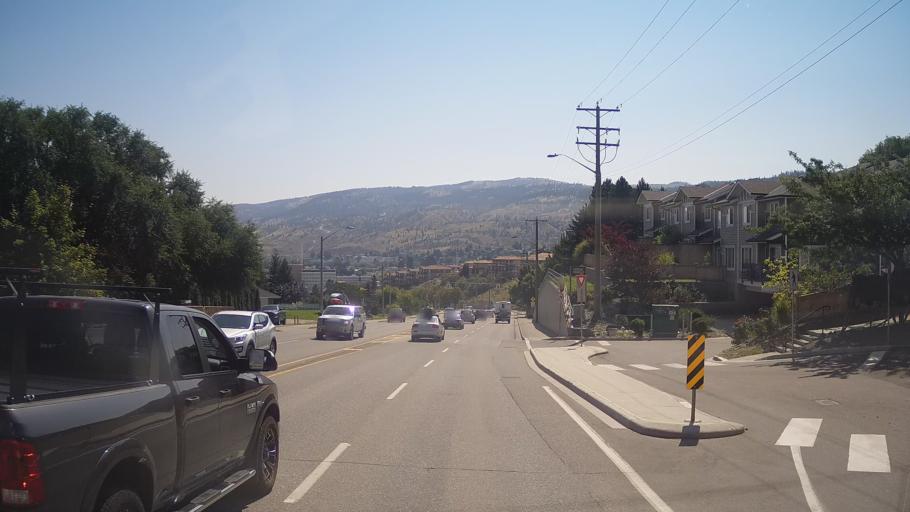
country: CA
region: British Columbia
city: Kamloops
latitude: 50.6735
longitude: -120.3473
